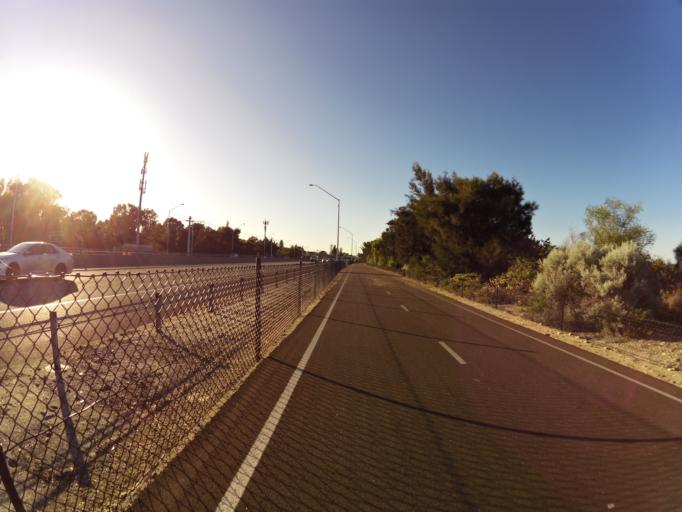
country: AU
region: Western Australia
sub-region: South Perth
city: Como
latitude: -31.9853
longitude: 115.8517
